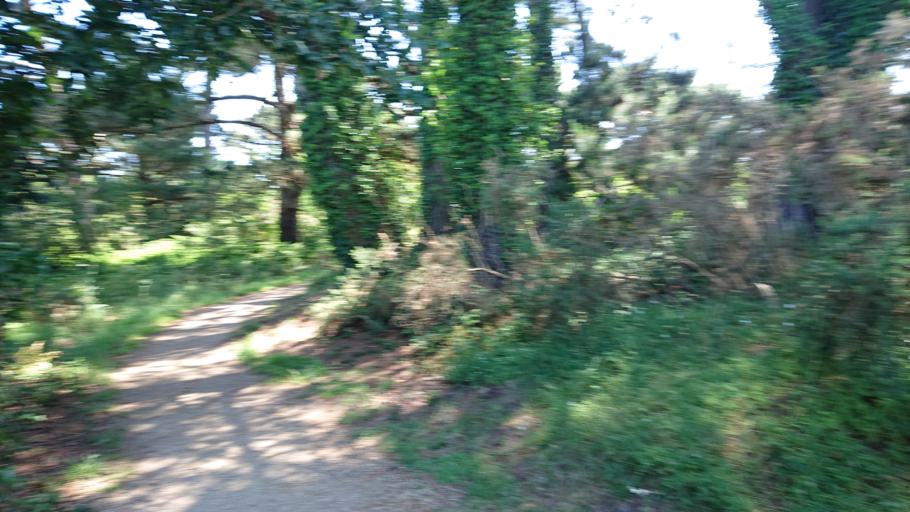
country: FR
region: Brittany
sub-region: Departement des Cotes-d'Armor
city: Tregastel
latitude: 48.8280
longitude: -3.4791
